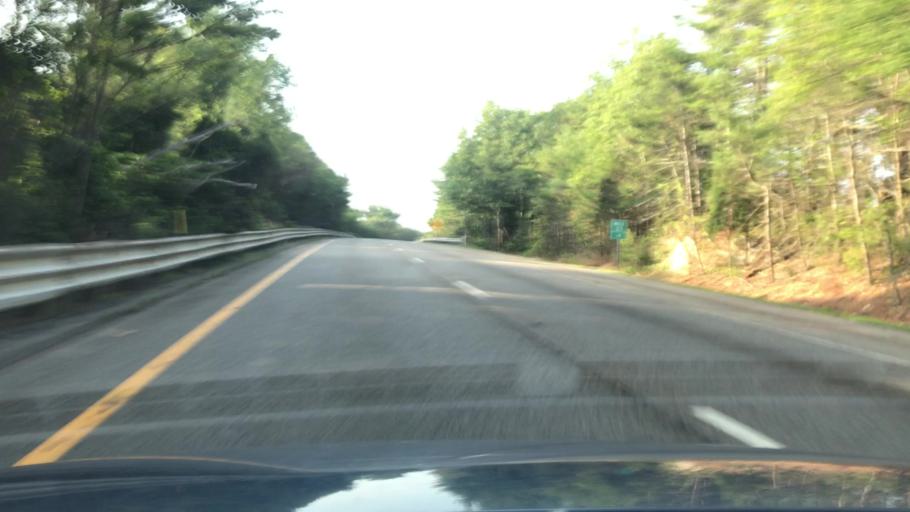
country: US
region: Massachusetts
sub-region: Plymouth County
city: Marshfield
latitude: 42.0677
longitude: -70.7298
